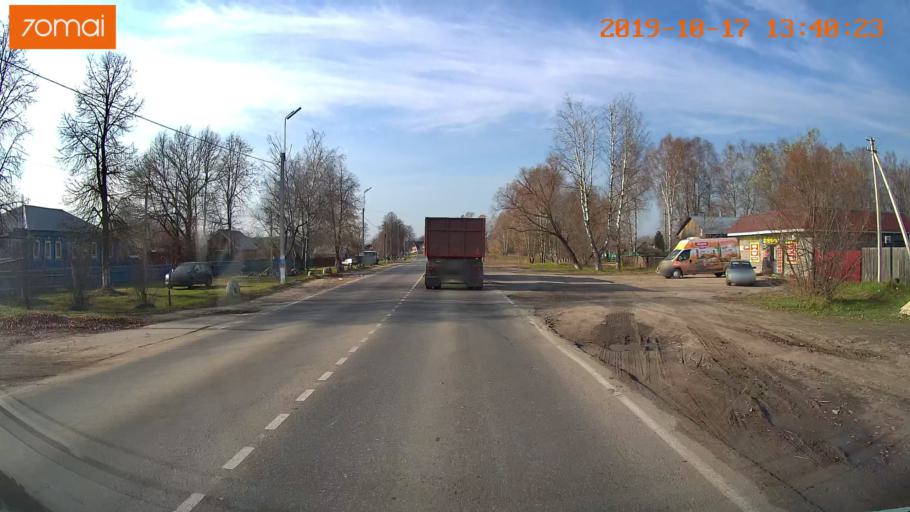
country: RU
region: Rjazan
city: Tuma
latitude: 55.1479
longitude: 40.5743
